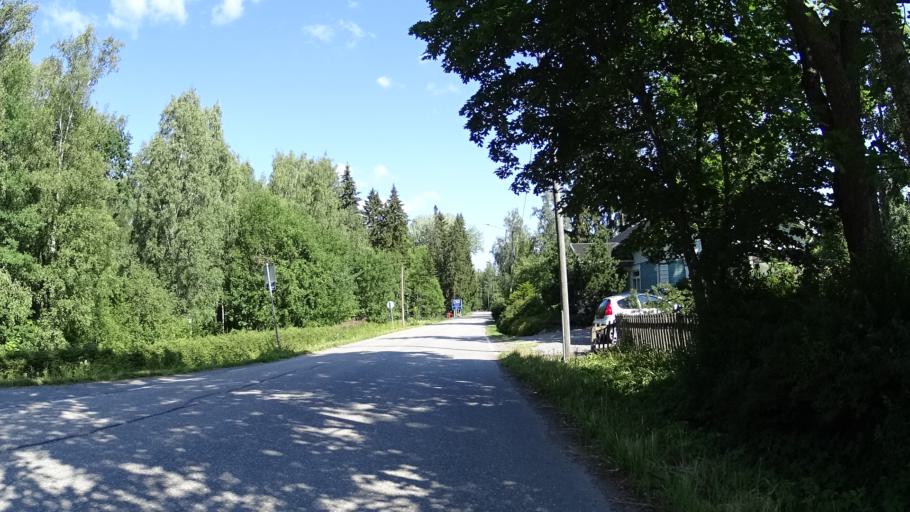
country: FI
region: Uusimaa
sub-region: Helsinki
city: Tuusula
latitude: 60.4237
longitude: 25.0482
